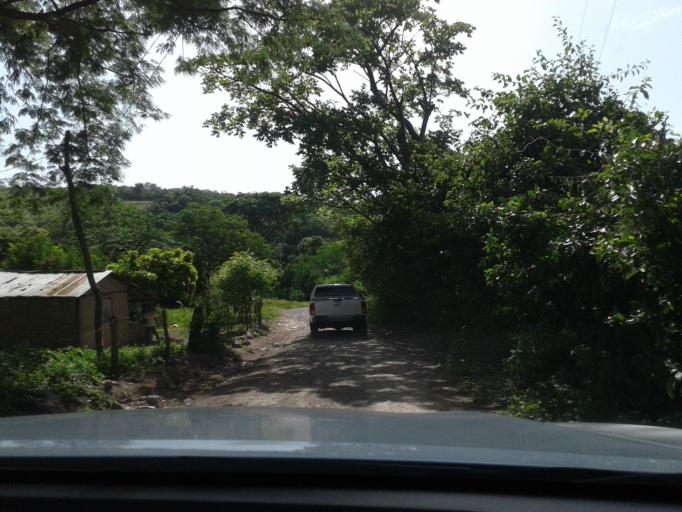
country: NI
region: Matagalpa
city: Terrabona
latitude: 12.5550
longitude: -86.0302
